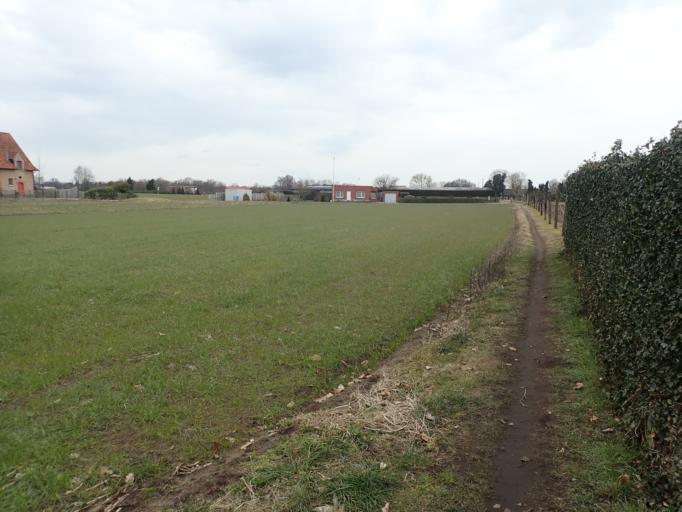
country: BE
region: Flanders
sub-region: Provincie Antwerpen
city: Nijlen
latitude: 51.1674
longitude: 4.6635
